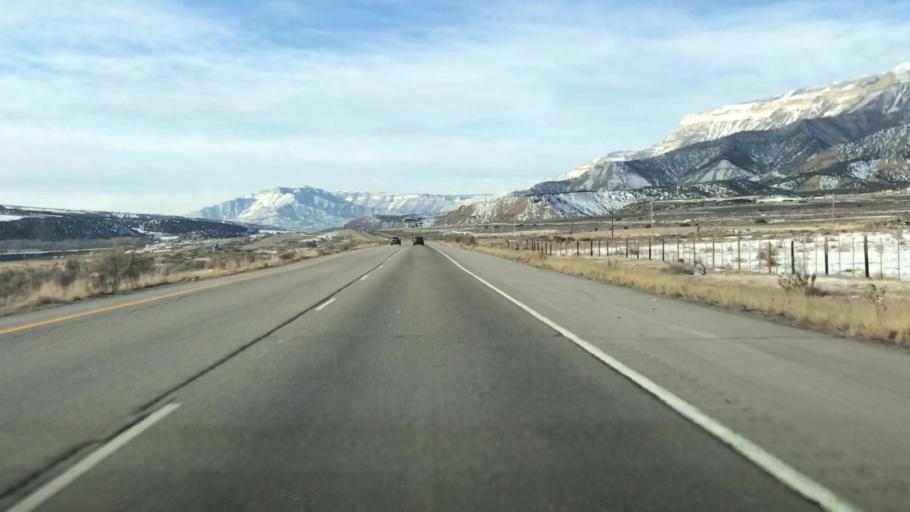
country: US
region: Colorado
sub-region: Garfield County
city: Rifle
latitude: 39.5054
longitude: -107.8937
